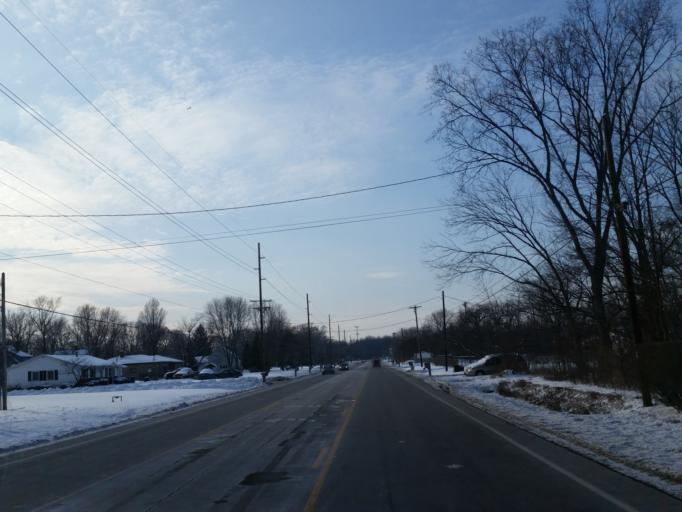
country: US
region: Ohio
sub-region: Lorain County
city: Sheffield Lake
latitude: 41.4614
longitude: -82.1161
